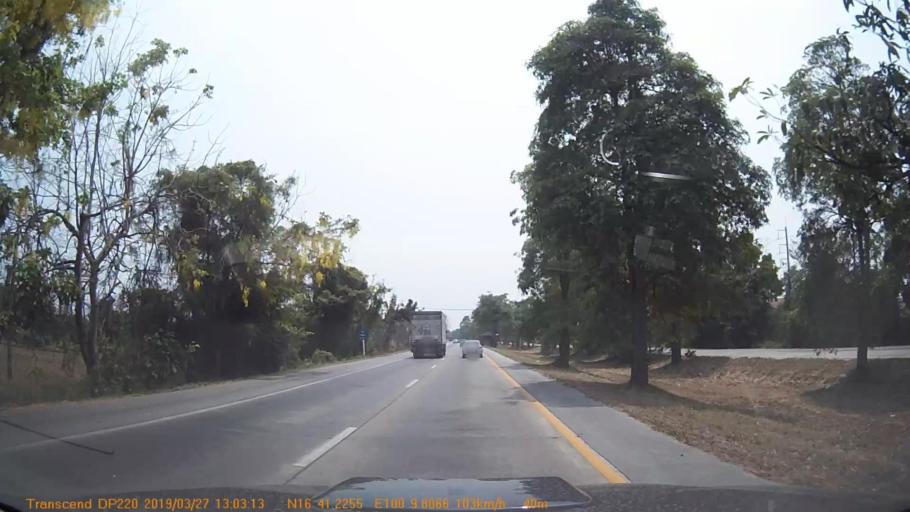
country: TH
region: Phitsanulok
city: Bang Rakam
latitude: 16.6869
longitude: 100.1634
